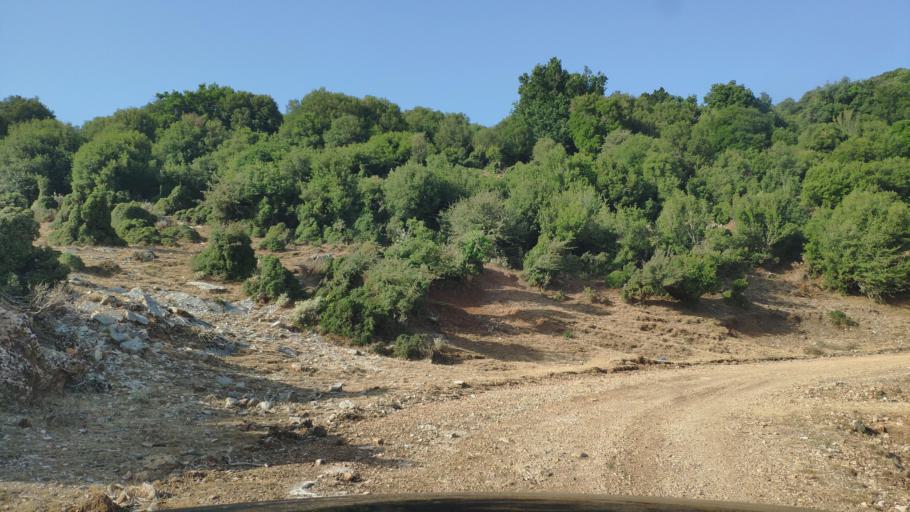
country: GR
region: West Greece
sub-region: Nomos Aitolias kai Akarnanias
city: Monastirakion
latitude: 38.8351
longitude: 20.9736
